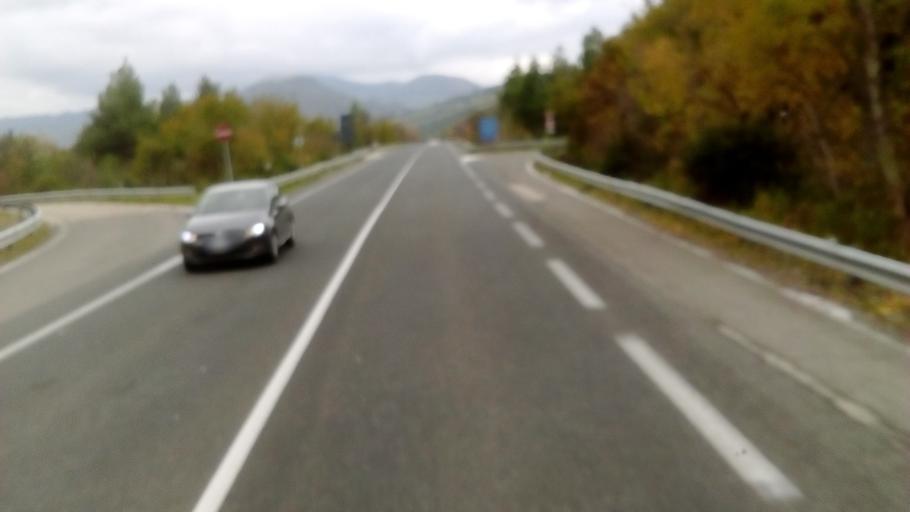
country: IT
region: Abruzzo
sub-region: Provincia di Chieti
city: San Giovanni Lipioni
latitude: 41.8279
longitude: 14.5741
